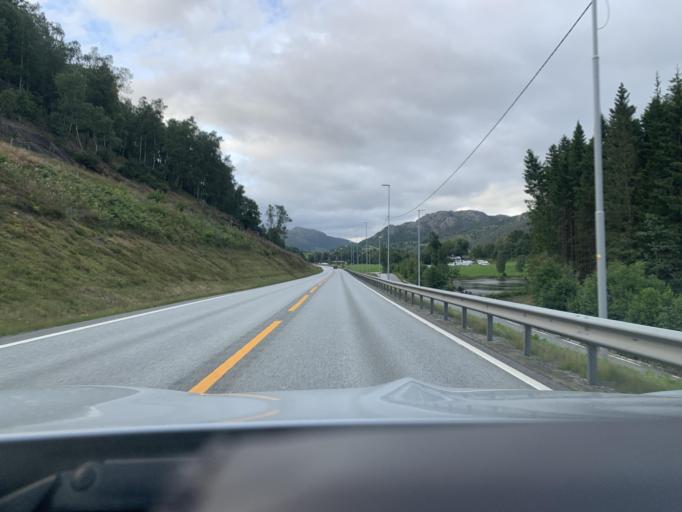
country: NO
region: Rogaland
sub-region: Bjerkreim
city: Vikesa
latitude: 58.5985
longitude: 6.0811
